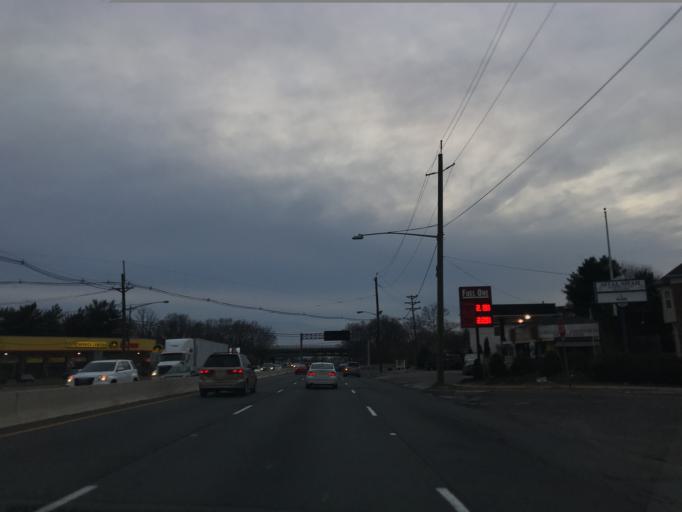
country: US
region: New Jersey
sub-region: Middlesex County
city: Piscataway
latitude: 40.5014
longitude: -74.4043
